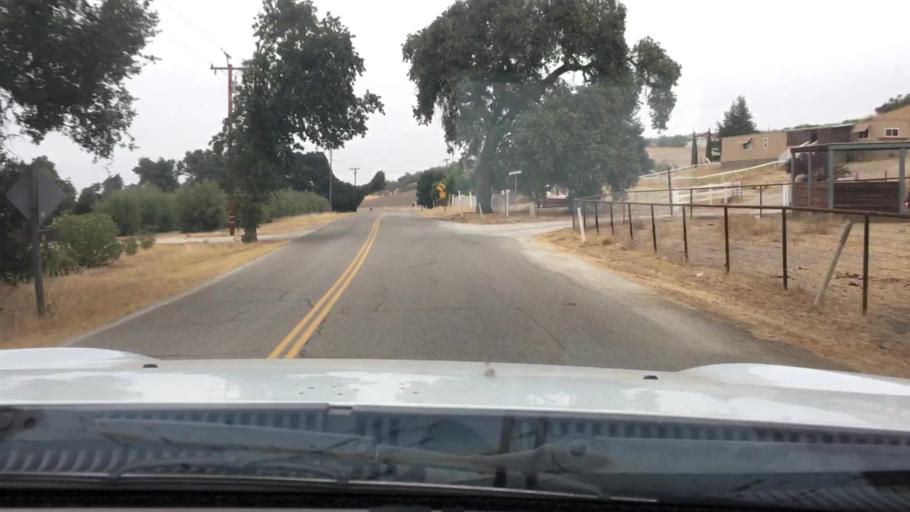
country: US
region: California
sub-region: San Luis Obispo County
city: Atascadero
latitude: 35.5310
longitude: -120.6164
